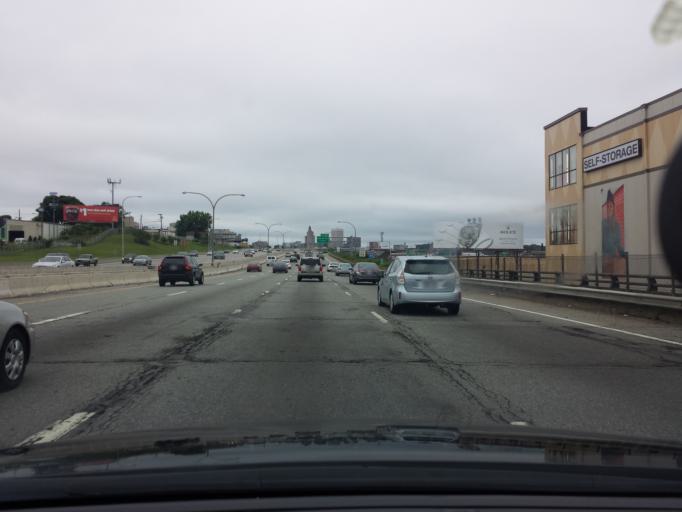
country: US
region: Rhode Island
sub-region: Providence County
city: Providence
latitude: 41.8038
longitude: -71.4039
